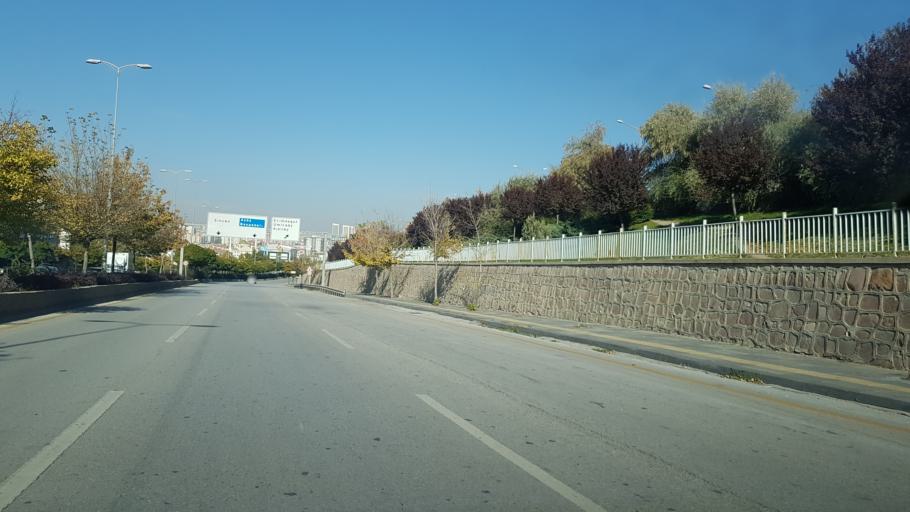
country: TR
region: Ankara
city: Etimesgut
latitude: 39.9558
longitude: 32.6048
